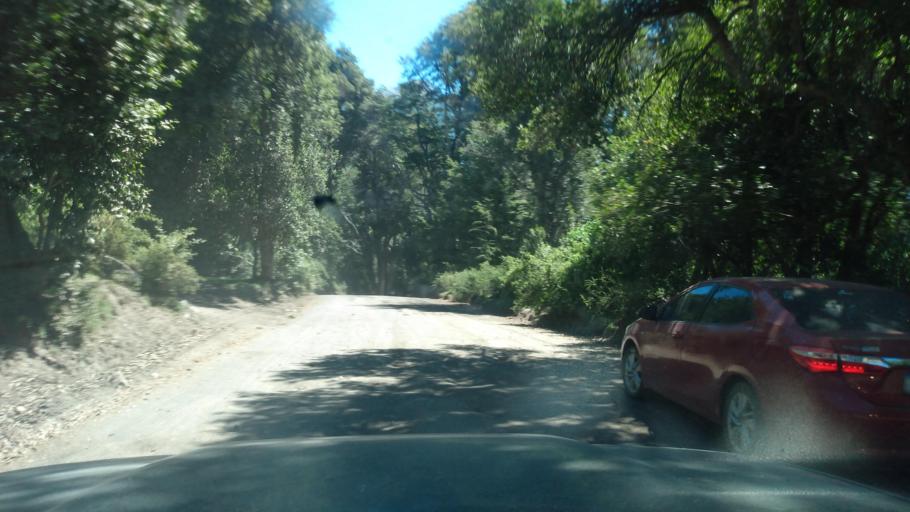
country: AR
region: Neuquen
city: Villa La Angostura
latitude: -40.6284
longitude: -71.4920
